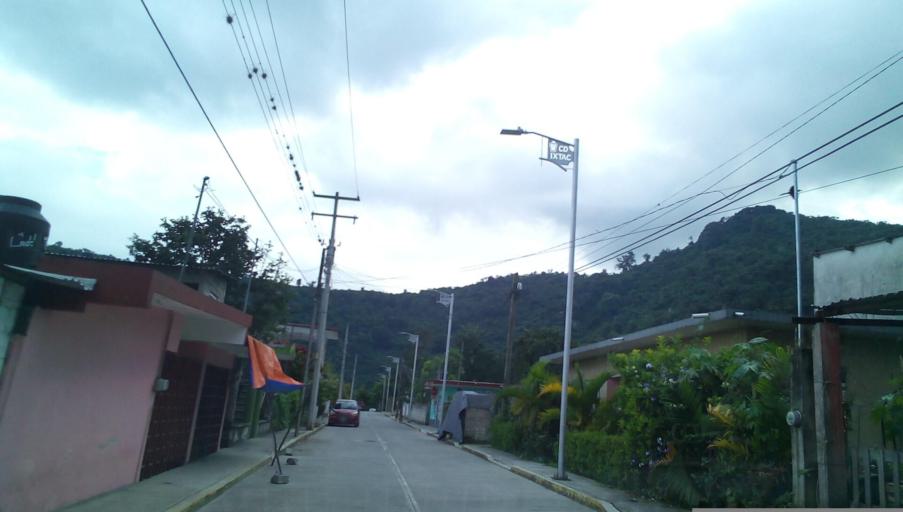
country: MX
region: Veracruz
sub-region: Ixtaczoquitlan
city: Buenavista
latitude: 18.8920
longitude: -97.0390
